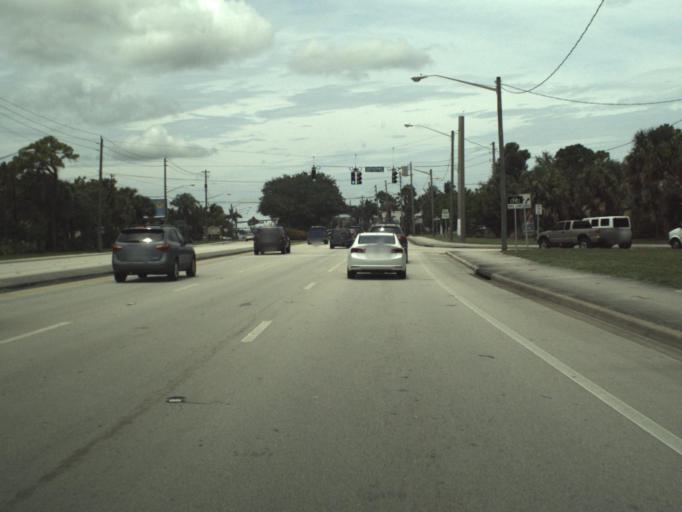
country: US
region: Florida
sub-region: Palm Beach County
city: Limestone Creek
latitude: 26.9345
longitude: -80.1275
